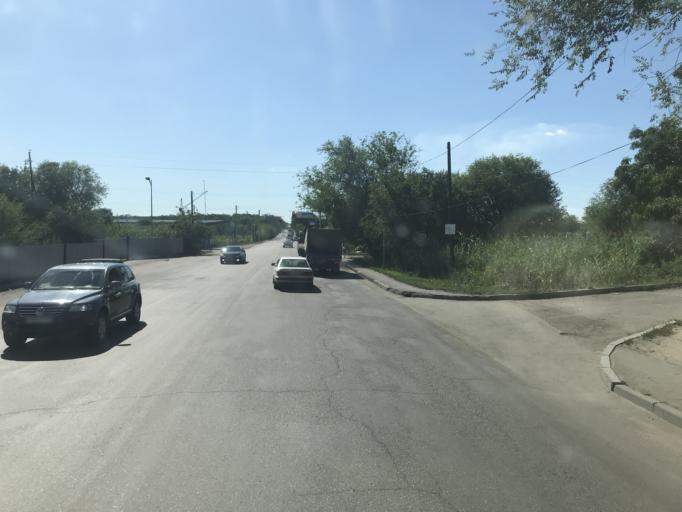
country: KZ
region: Almaty Oblysy
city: Pervomayskiy
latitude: 43.3545
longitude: 76.9166
